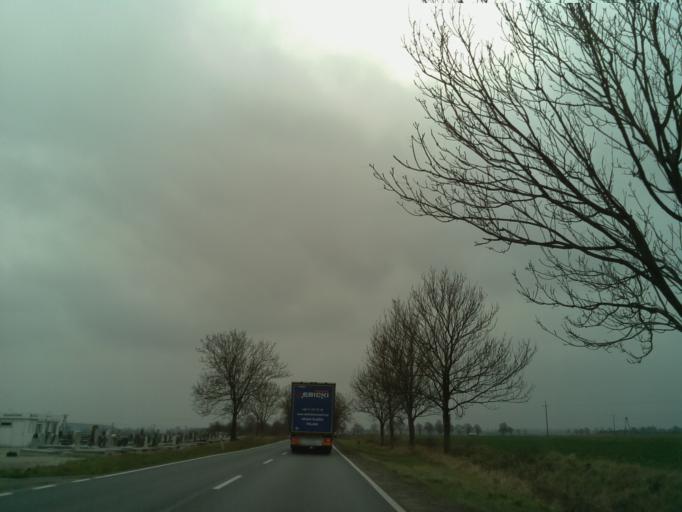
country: PL
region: Lower Silesian Voivodeship
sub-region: Powiat swidnicki
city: Stanowice
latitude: 50.9466
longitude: 16.3639
